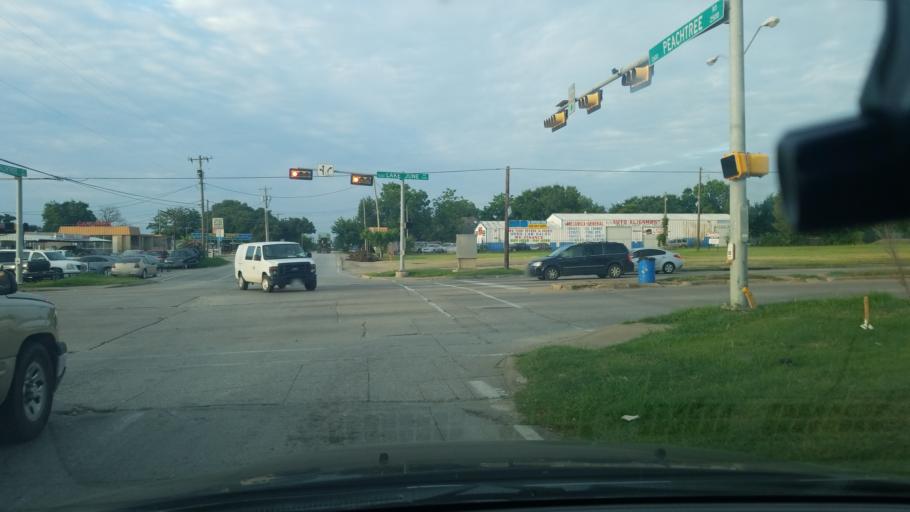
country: US
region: Texas
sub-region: Dallas County
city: Balch Springs
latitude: 32.7343
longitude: -96.6313
